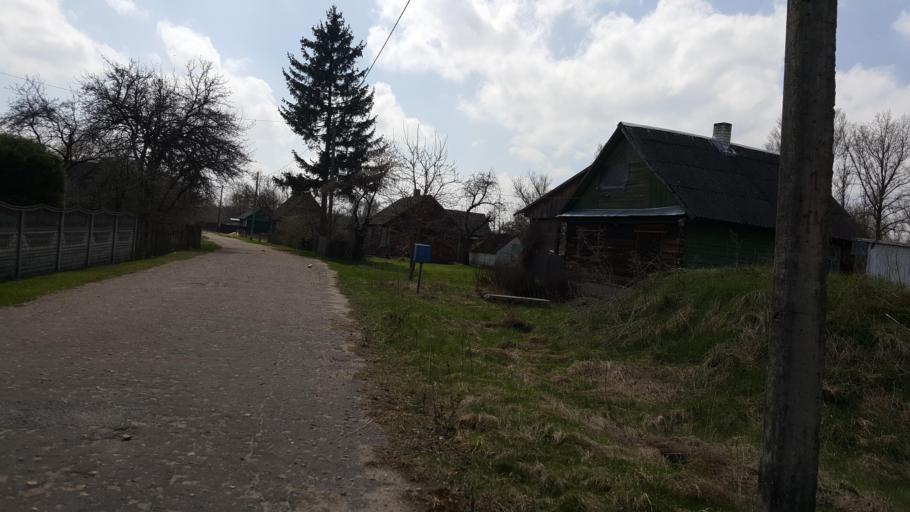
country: BY
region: Brest
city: Zhabinka
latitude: 52.2553
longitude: 23.9648
